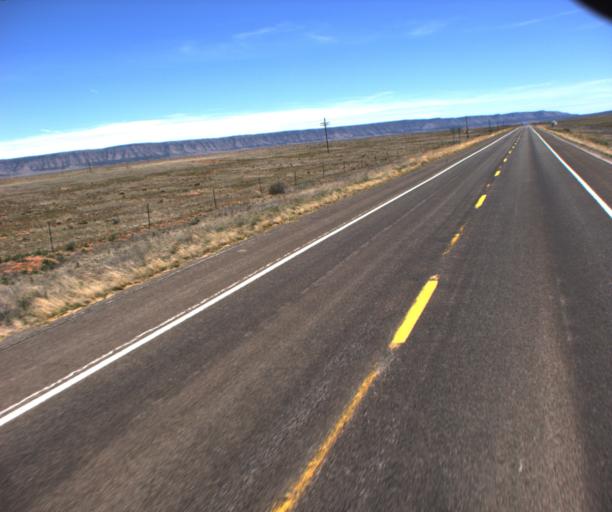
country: US
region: Arizona
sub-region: Mohave County
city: Peach Springs
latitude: 35.4685
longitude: -113.1224
